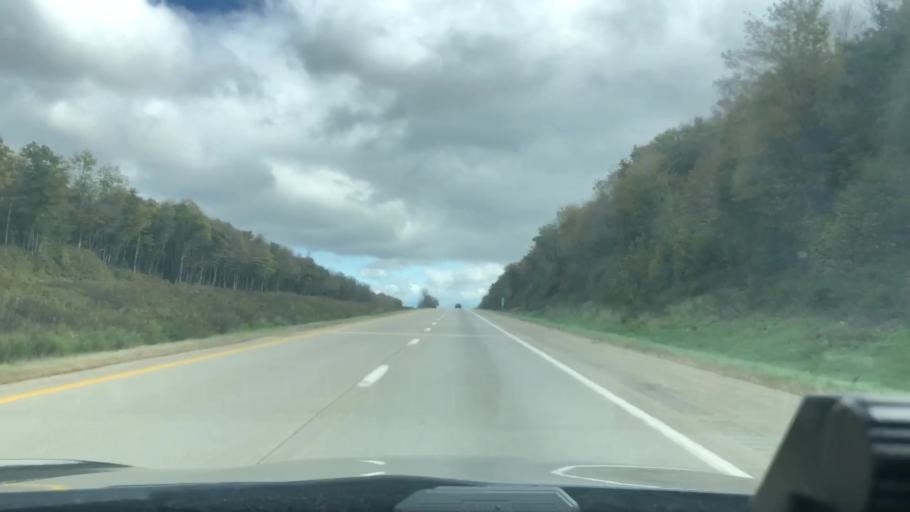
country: US
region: Pennsylvania
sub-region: Monroe County
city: Pocono Pines
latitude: 41.2137
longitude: -75.4733
